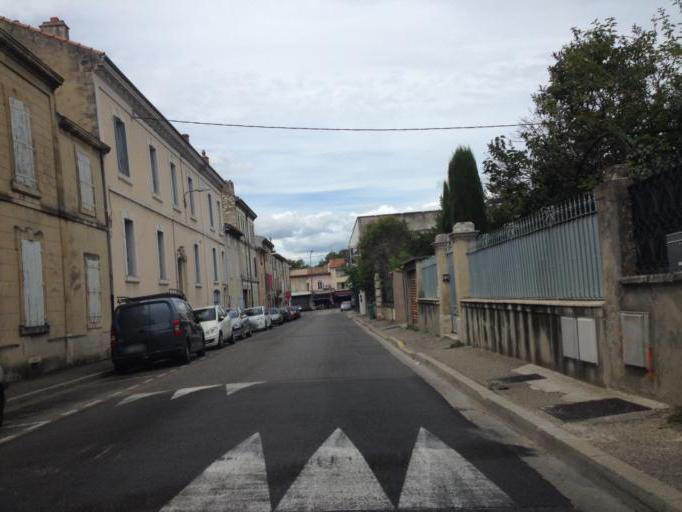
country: FR
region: Rhone-Alpes
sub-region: Departement de la Drome
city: Montelimar
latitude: 44.5503
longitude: 4.7490
